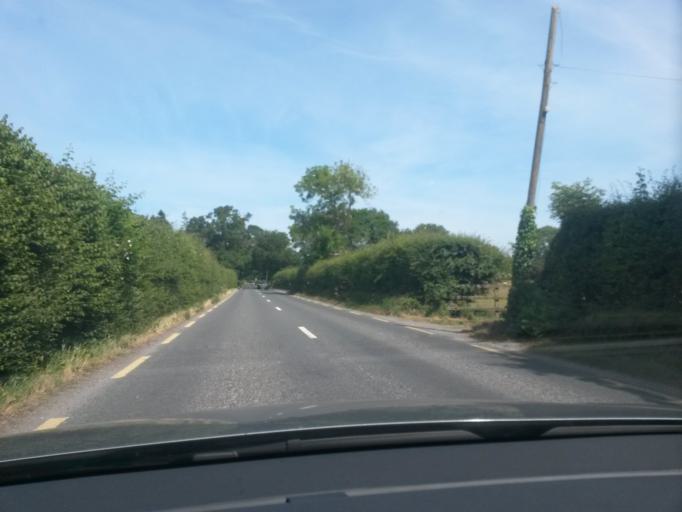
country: IE
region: Leinster
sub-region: Kildare
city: Eadestown
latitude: 53.2003
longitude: -6.6029
